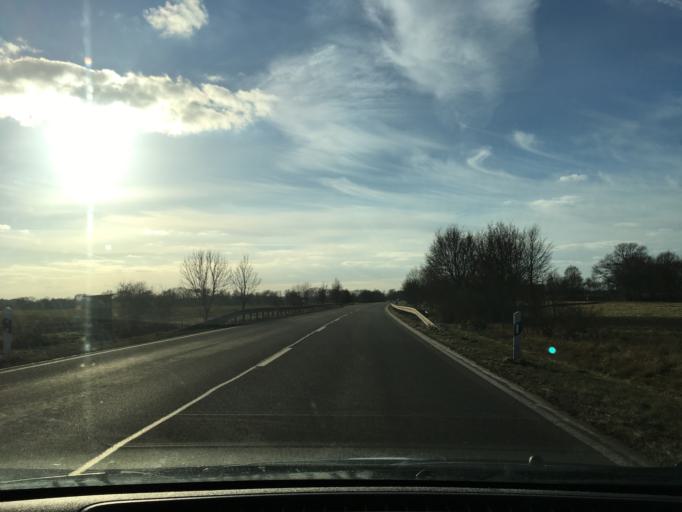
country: DE
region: Saxony-Anhalt
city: Luftkurort Arendsee
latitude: 52.8804
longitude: 11.5246
